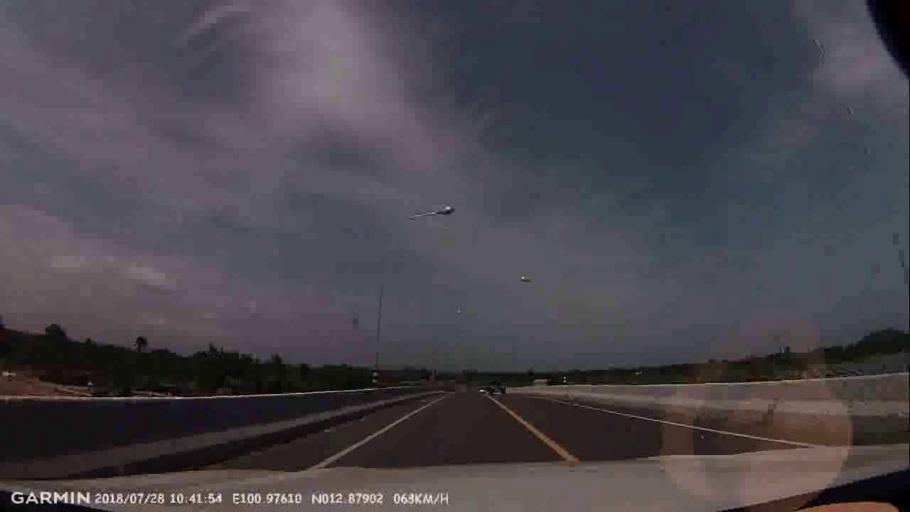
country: TH
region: Chon Buri
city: Phatthaya
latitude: 12.8780
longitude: 100.9760
